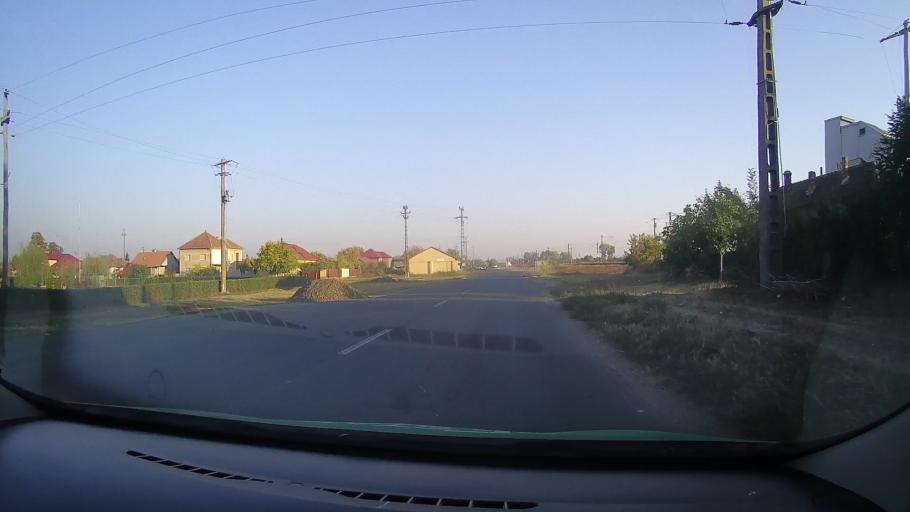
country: RO
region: Arad
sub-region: Comuna Sofronea
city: Sofronea
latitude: 46.2773
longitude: 21.3141
